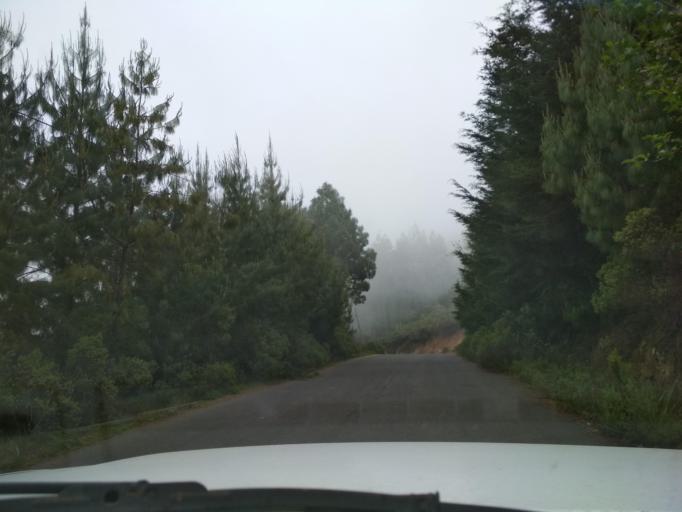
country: MX
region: Veracruz
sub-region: Mariano Escobedo
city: Loma Grande
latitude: 18.9305
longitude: -97.2211
